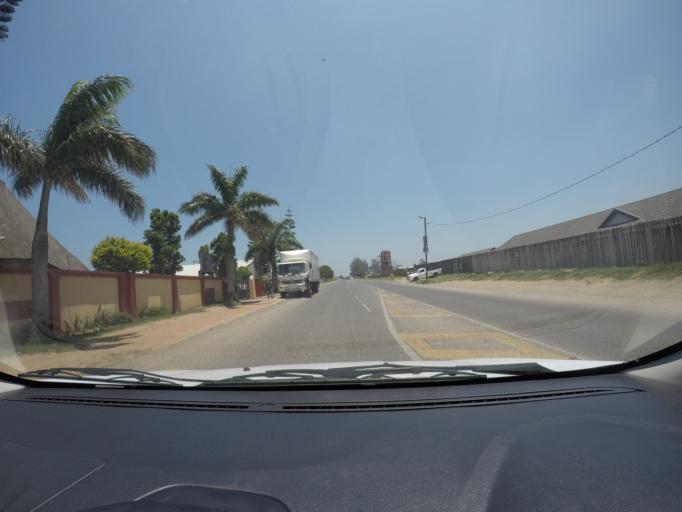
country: ZA
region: KwaZulu-Natal
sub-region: uThungulu District Municipality
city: eSikhawini
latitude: -28.8882
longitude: 31.8962
